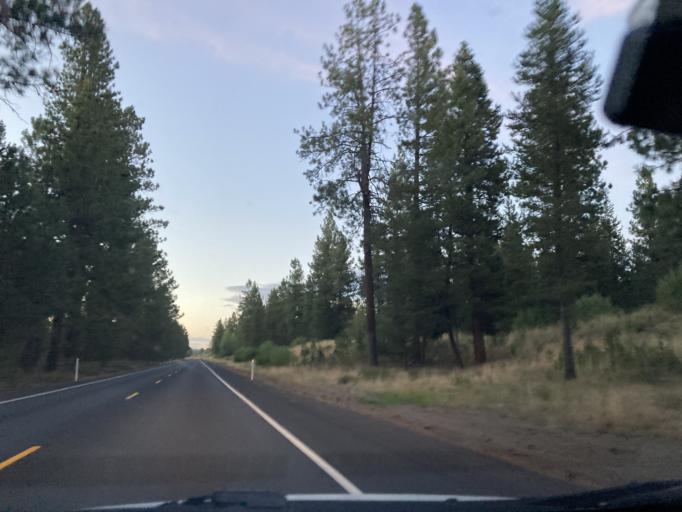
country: US
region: Oregon
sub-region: Deschutes County
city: Three Rivers
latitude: 43.8429
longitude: -121.4414
